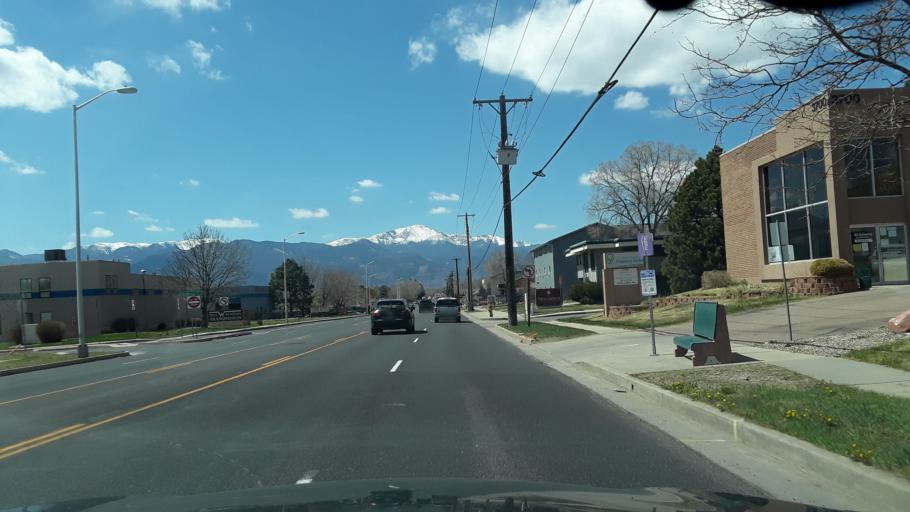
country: US
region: Colorado
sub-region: El Paso County
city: Cimarron Hills
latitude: 38.8472
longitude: -104.7592
